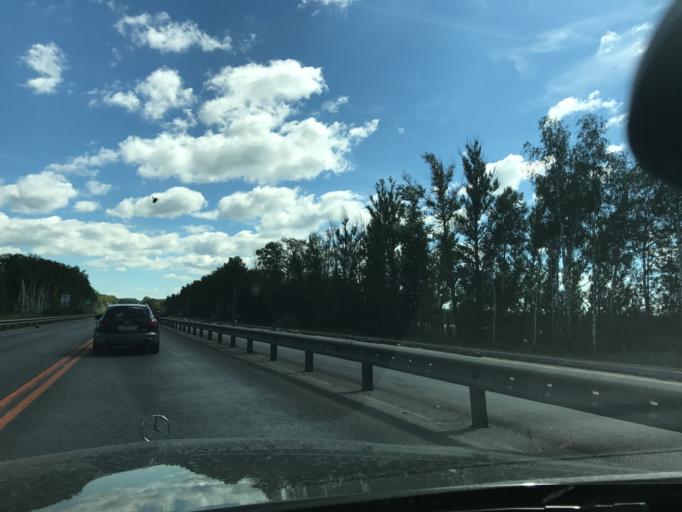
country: RU
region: Vladimir
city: Novovyazniki
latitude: 56.2114
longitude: 42.2657
